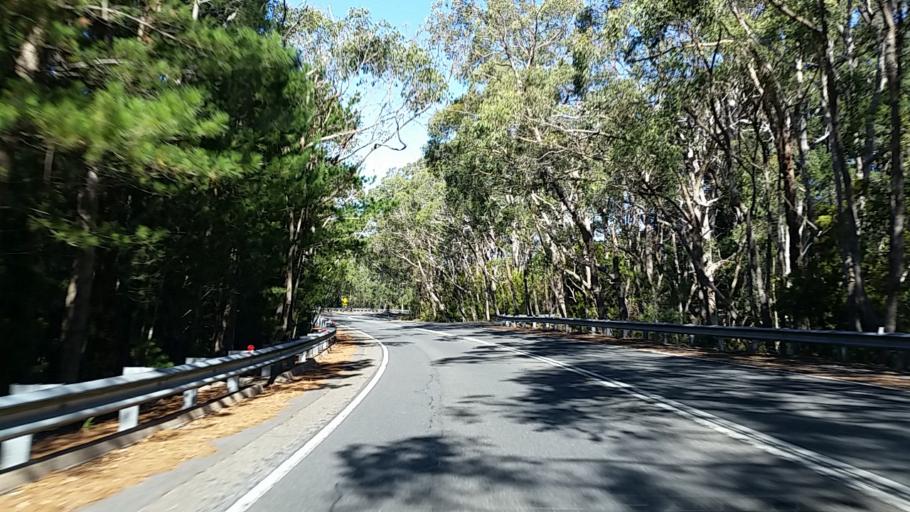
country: AU
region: South Australia
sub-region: Adelaide Hills
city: Crafers
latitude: -34.9909
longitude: 138.7082
